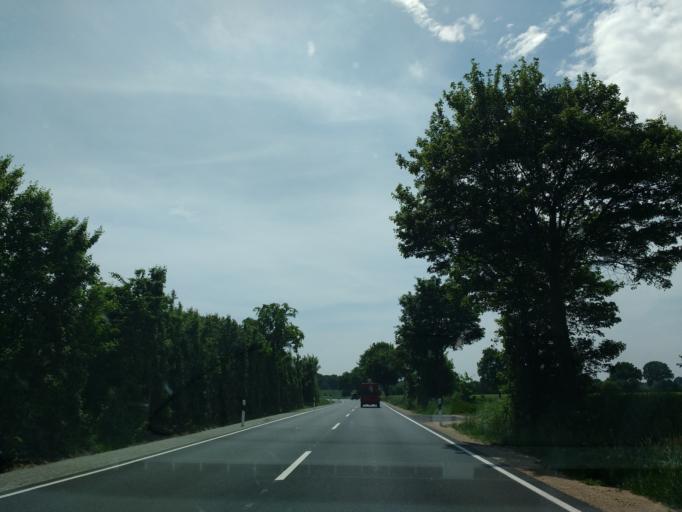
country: DE
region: Schleswig-Holstein
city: Braak
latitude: 53.6056
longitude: 10.2413
